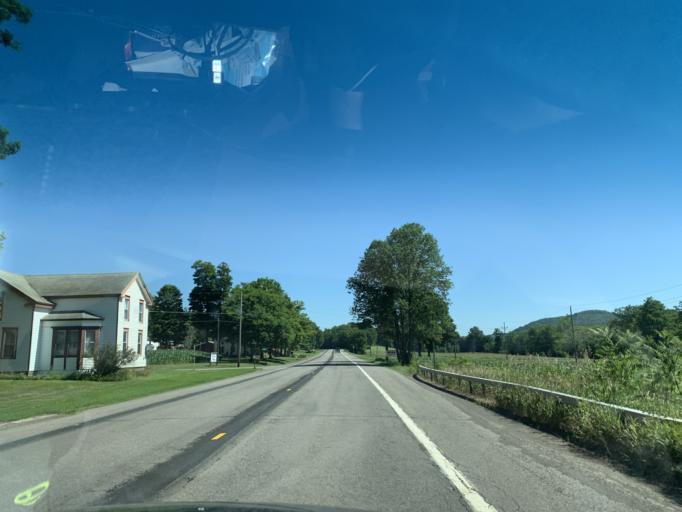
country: US
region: New York
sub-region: Delaware County
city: Sidney
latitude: 42.3929
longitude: -75.4003
